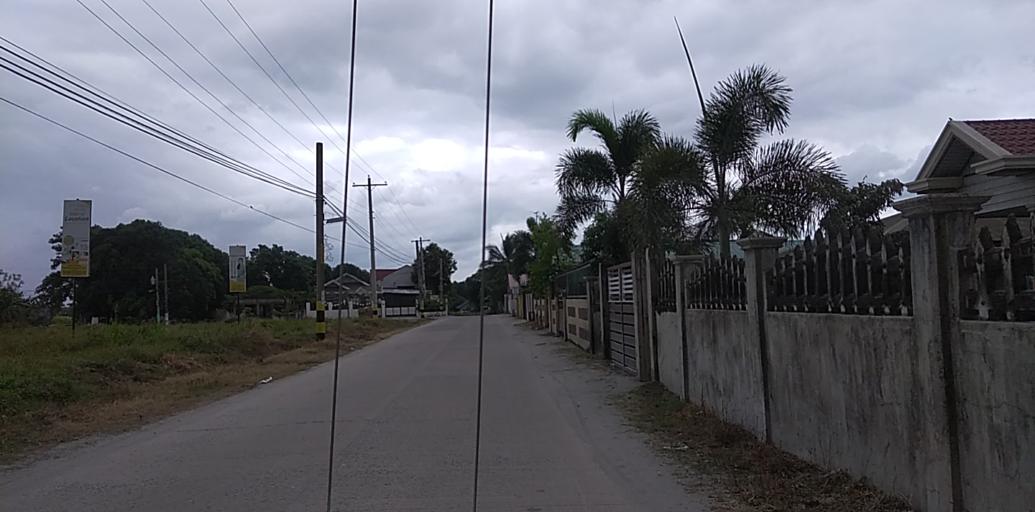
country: PH
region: Central Luzon
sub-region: Province of Pampanga
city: Pio
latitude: 15.0454
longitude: 120.5327
